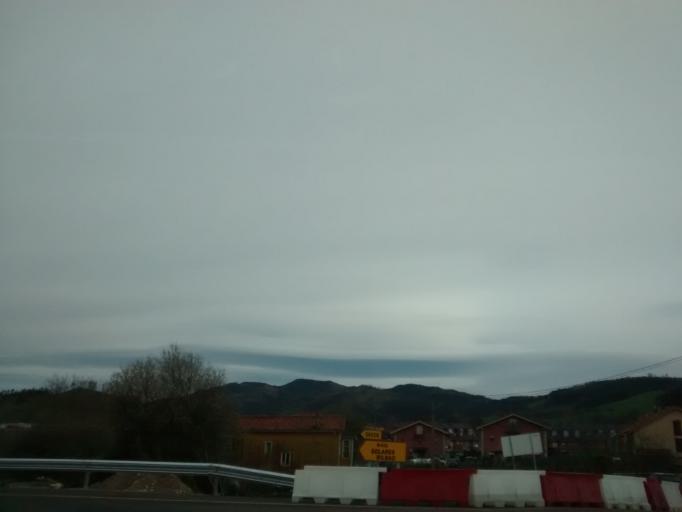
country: ES
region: Cantabria
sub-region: Provincia de Cantabria
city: Puente Viesgo
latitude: 43.3150
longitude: -3.9501
